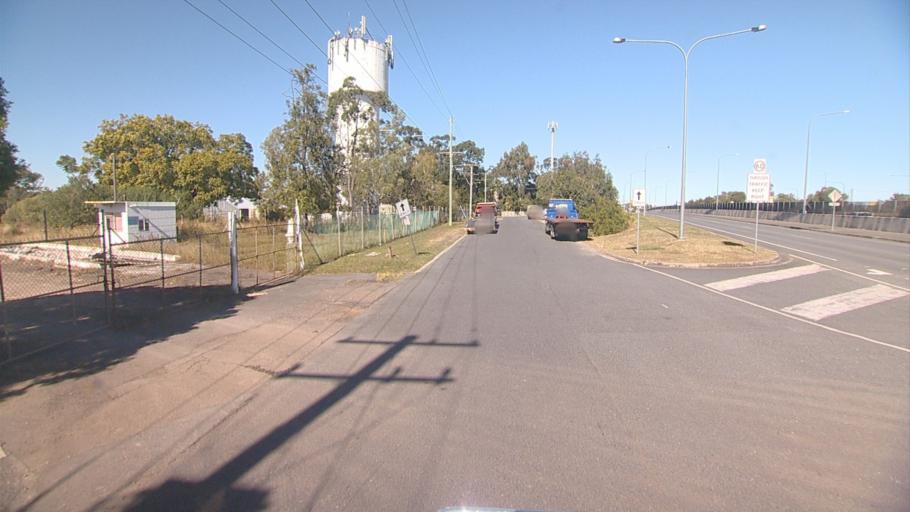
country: AU
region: Queensland
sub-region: Logan
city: Park Ridge South
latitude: -27.7039
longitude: 153.0387
